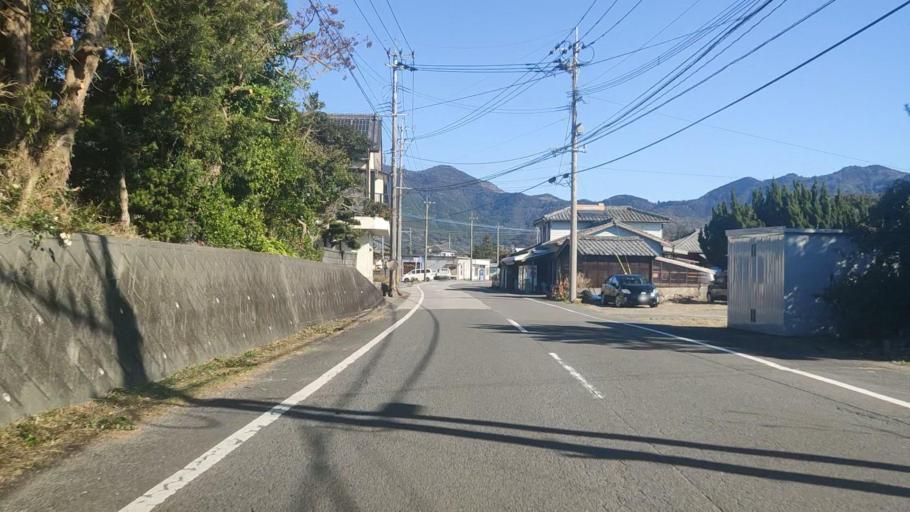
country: JP
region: Oita
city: Saiki
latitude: 32.8040
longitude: 131.8887
